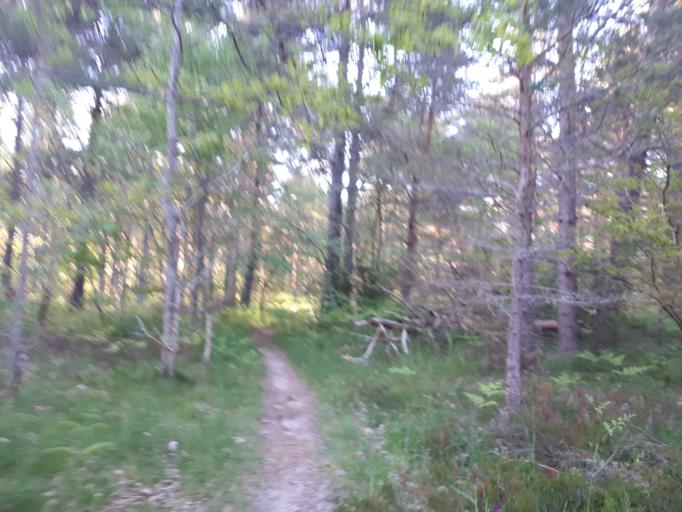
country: SE
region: Gotland
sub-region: Gotland
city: Visby
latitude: 57.6077
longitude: 18.2881
